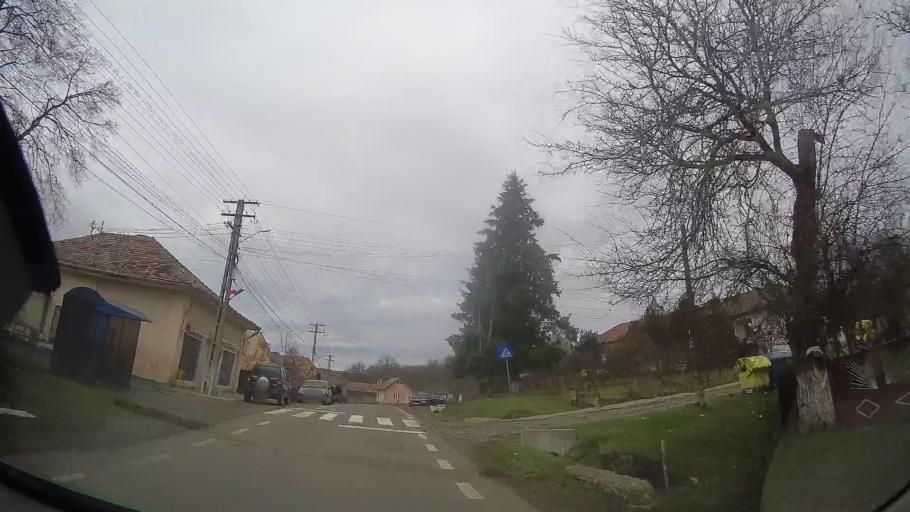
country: RO
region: Mures
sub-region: Comuna Cozma
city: Cozma
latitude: 46.8088
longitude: 24.5208
